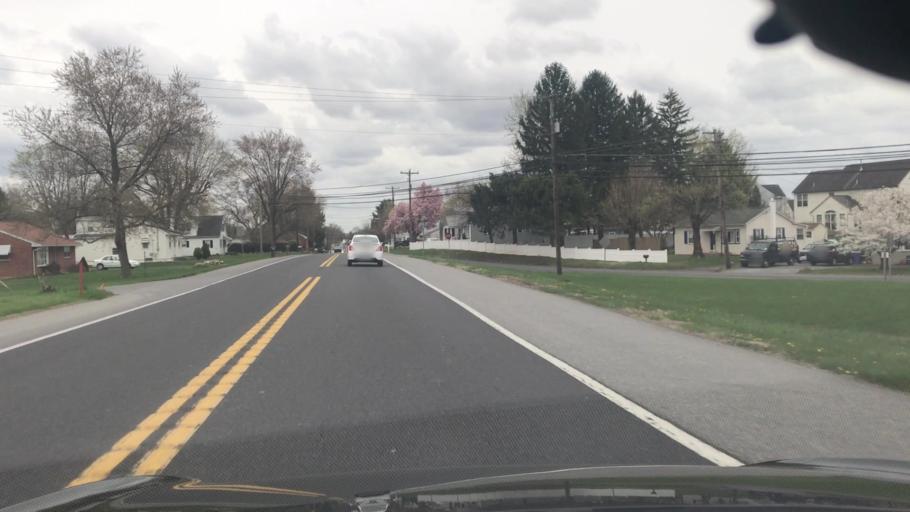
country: US
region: Pennsylvania
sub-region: Cumberland County
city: Mechanicsburg
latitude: 40.2281
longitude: -77.0297
